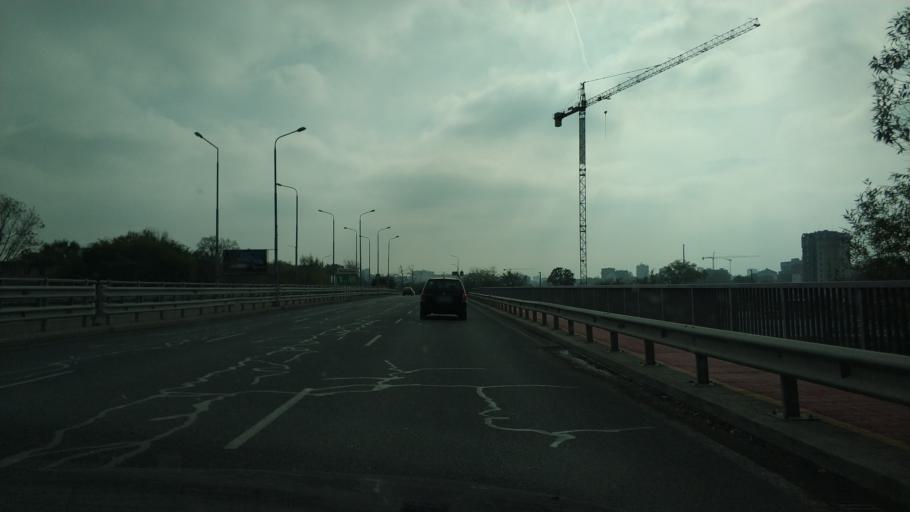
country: BG
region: Plovdiv
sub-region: Obshtina Plovdiv
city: Plovdiv
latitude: 42.1550
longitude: 24.7656
